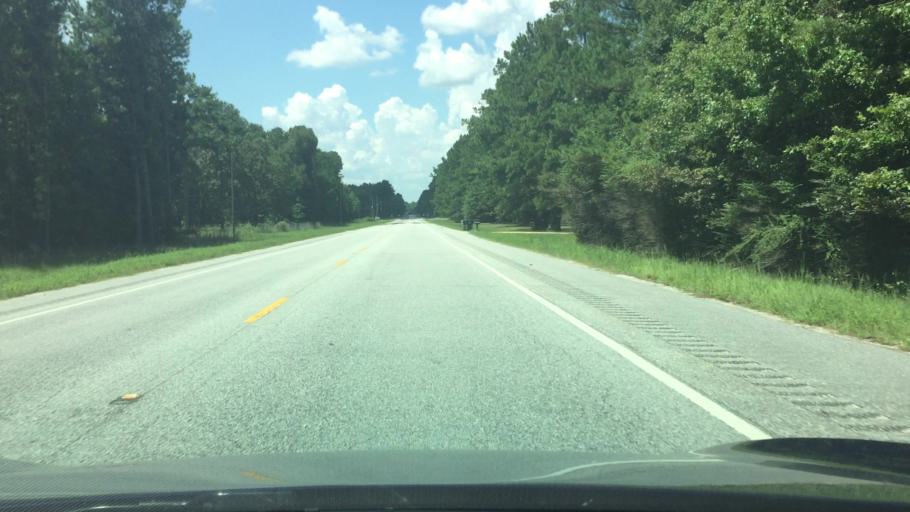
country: US
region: Alabama
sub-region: Montgomery County
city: Pike Road
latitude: 32.3850
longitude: -85.9863
